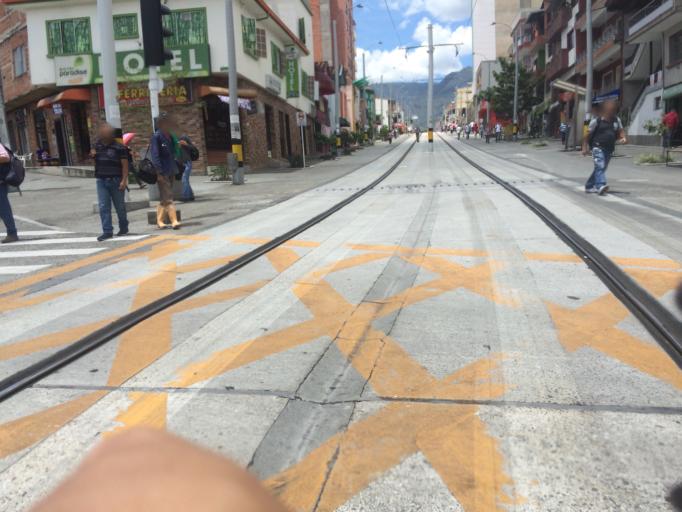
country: CO
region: Antioquia
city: Medellin
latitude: 6.2437
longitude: -75.5584
